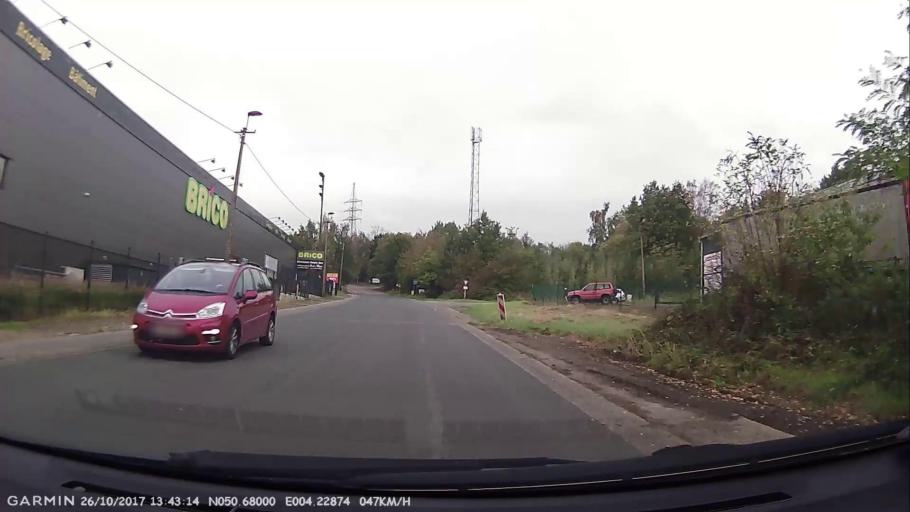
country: BE
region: Wallonia
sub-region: Province du Brabant Wallon
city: Tubize
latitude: 50.6799
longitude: 4.2287
